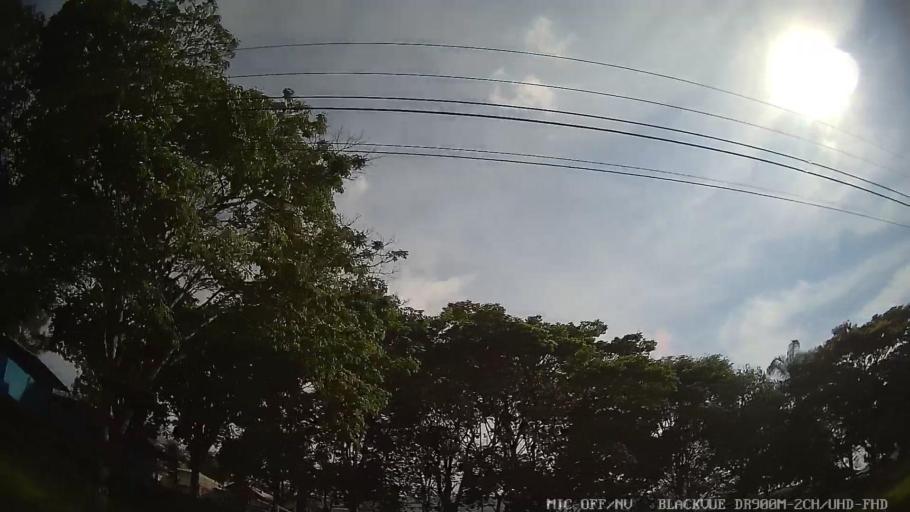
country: BR
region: Sao Paulo
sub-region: Braganca Paulista
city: Braganca Paulista
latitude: -22.9133
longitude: -46.5430
